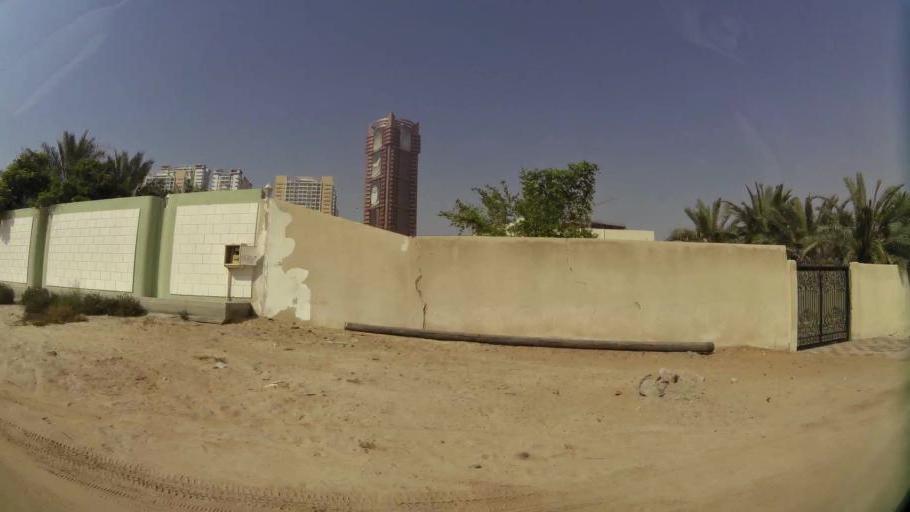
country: AE
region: Ajman
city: Ajman
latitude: 25.3910
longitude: 55.4284
